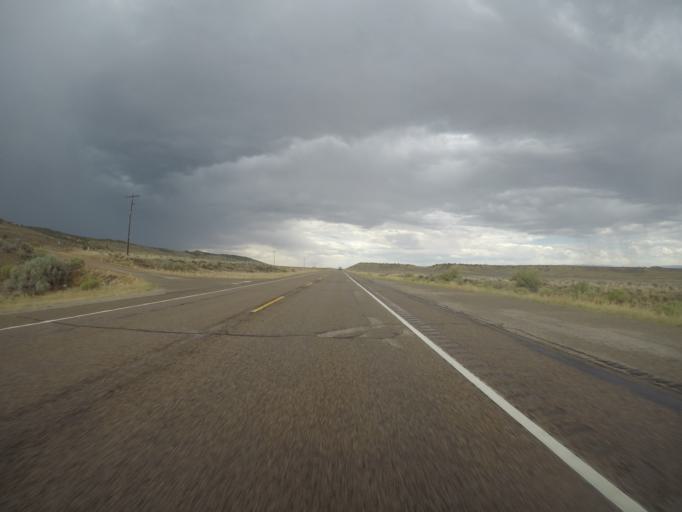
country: US
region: Colorado
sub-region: Rio Blanco County
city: Rangely
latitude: 40.2418
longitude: -108.9414
